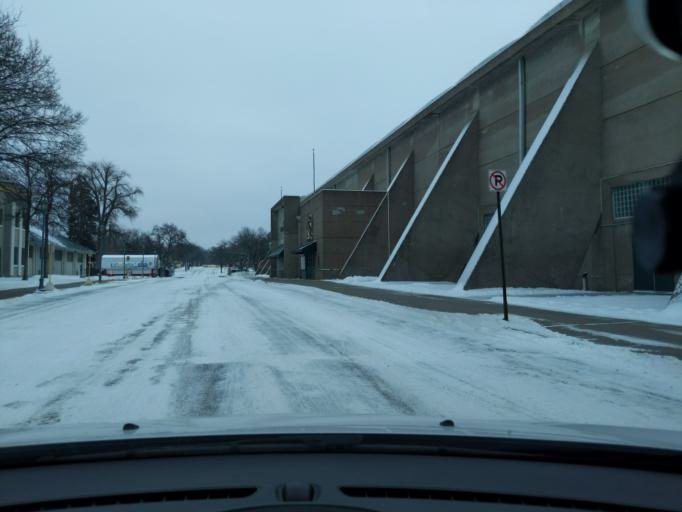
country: US
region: Minnesota
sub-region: Ramsey County
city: Falcon Heights
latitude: 44.9786
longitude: -93.1752
